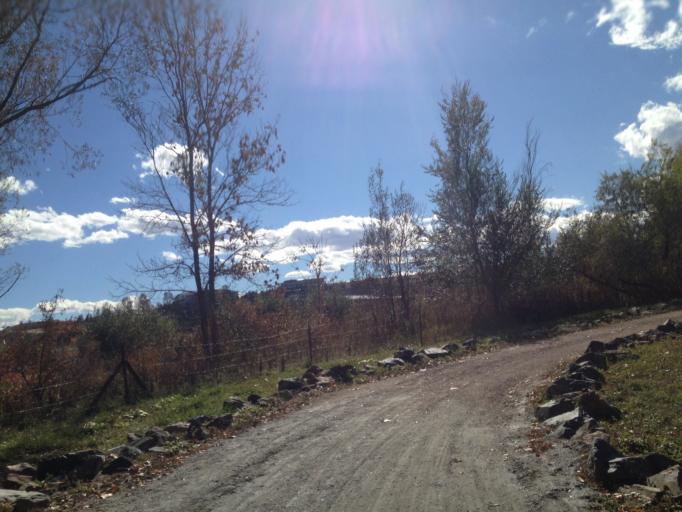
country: US
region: Colorado
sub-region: Boulder County
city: Superior
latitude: 39.9542
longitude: -105.1629
